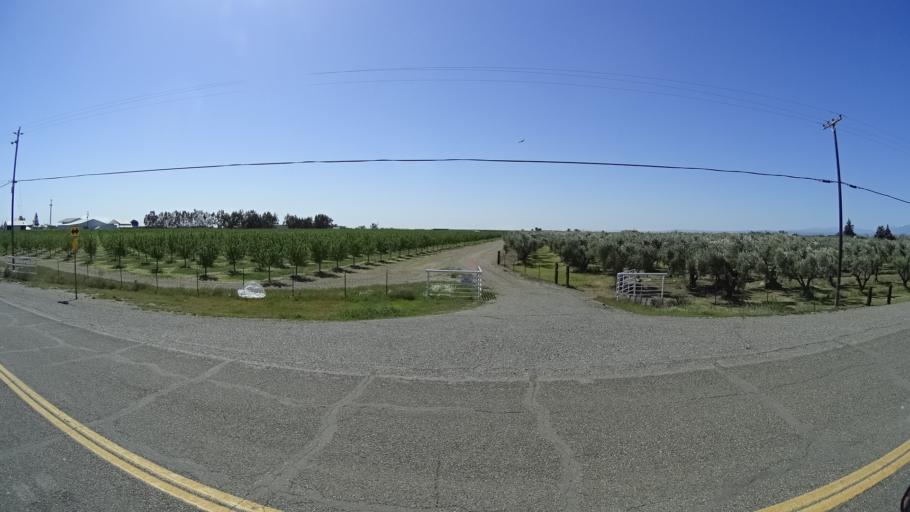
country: US
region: California
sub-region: Glenn County
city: Orland
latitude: 39.6969
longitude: -122.2037
